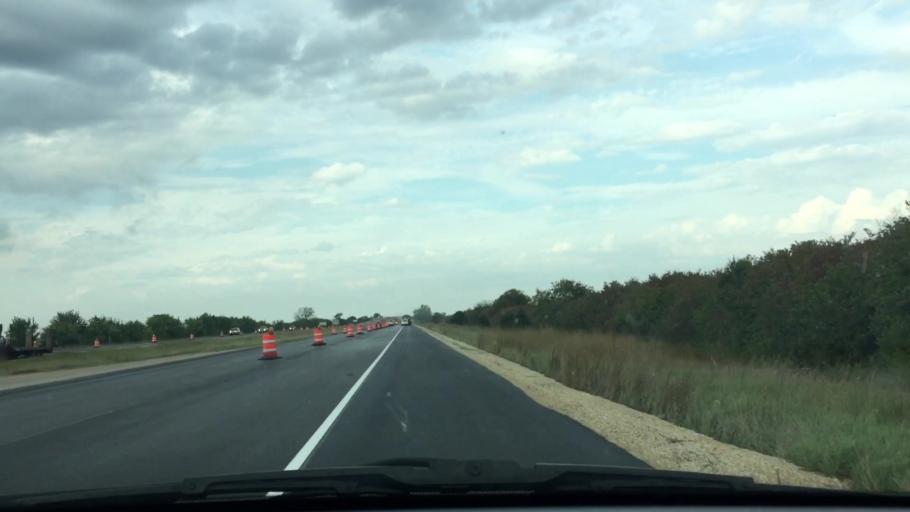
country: US
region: Illinois
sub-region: Whiteside County
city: Prophetstown
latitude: 41.7185
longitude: -89.9840
